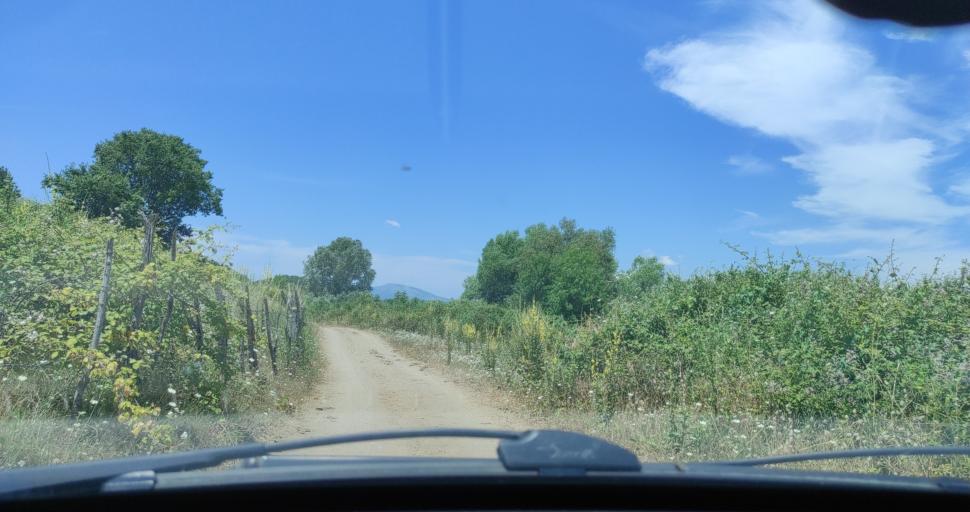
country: AL
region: Shkoder
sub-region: Rrethi i Shkodres
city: Velipoje
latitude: 41.8833
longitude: 19.3905
